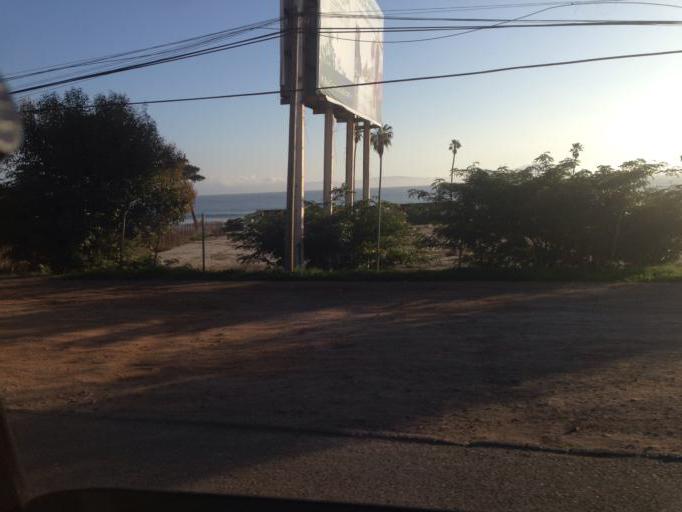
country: MX
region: Baja California
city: El Sauzal
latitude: 31.8625
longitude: -116.6525
